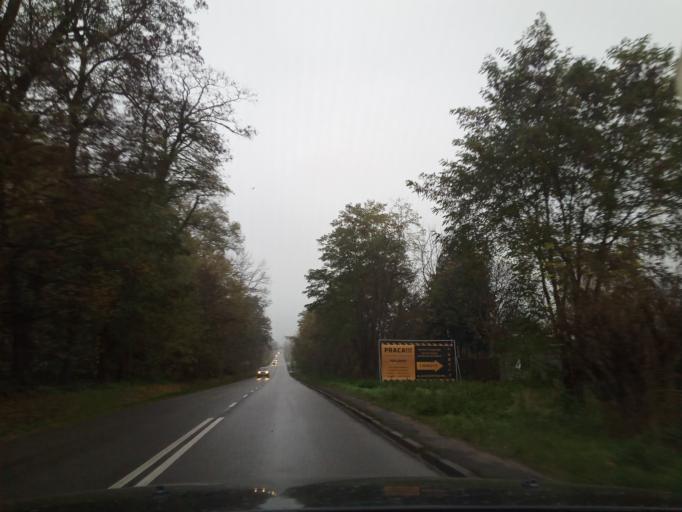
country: PL
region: Lesser Poland Voivodeship
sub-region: Powiat wielicki
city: Kokotow
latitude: 50.0996
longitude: 20.0675
